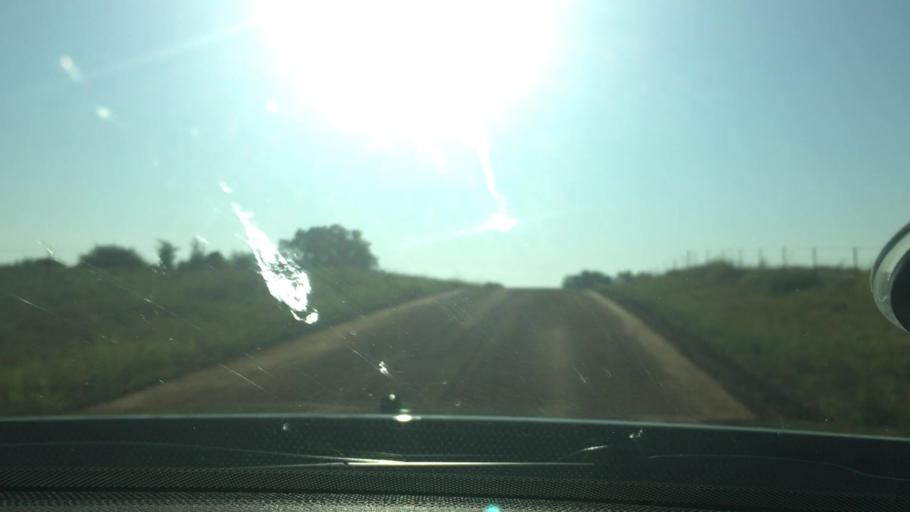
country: US
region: Oklahoma
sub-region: Murray County
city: Sulphur
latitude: 34.4193
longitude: -96.7877
